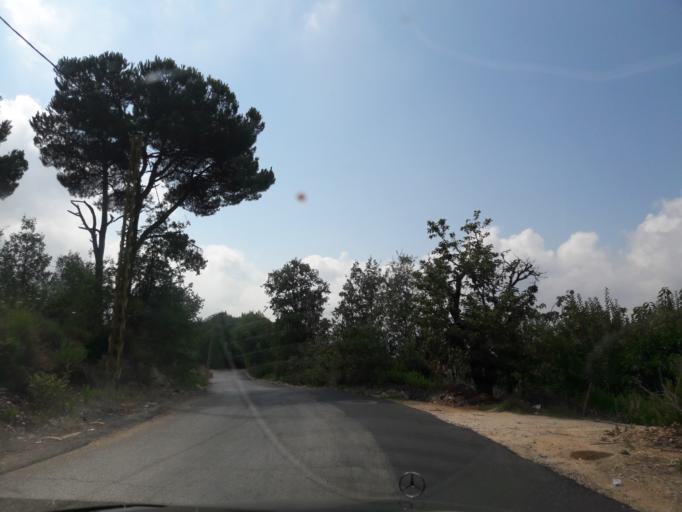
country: LB
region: Mont-Liban
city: Djounie
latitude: 33.9515
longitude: 35.7756
